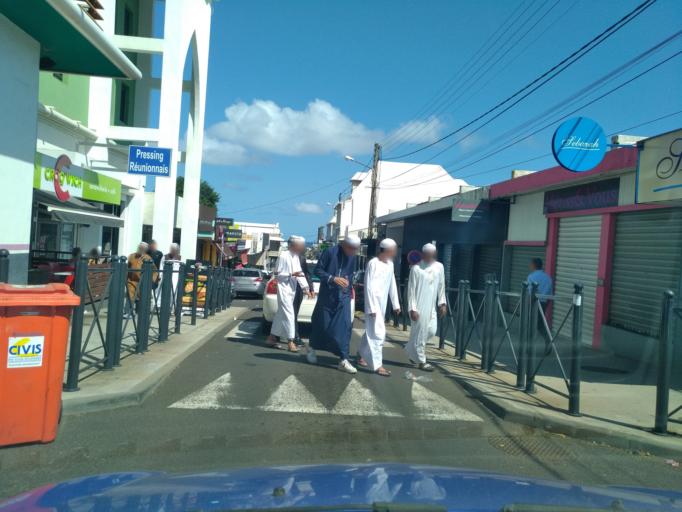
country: RE
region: Reunion
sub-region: Reunion
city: Saint-Pierre
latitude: -21.3390
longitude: 55.4746
